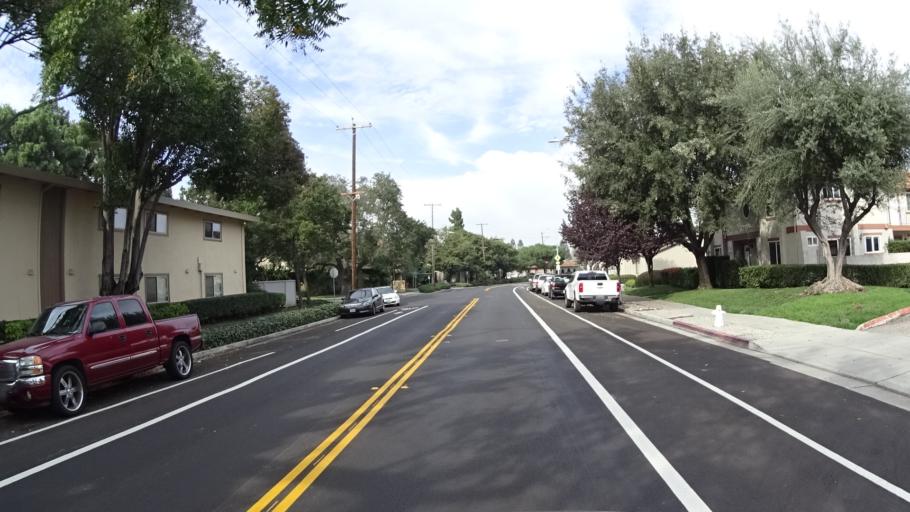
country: US
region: California
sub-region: Santa Clara County
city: Burbank
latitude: 37.3438
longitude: -121.9360
